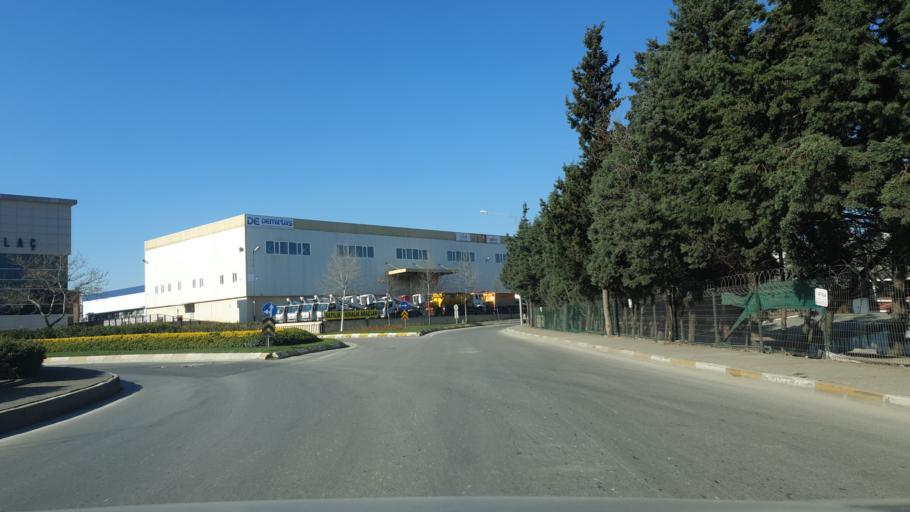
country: TR
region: Kocaeli
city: Balcik
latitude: 40.8783
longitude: 29.3672
